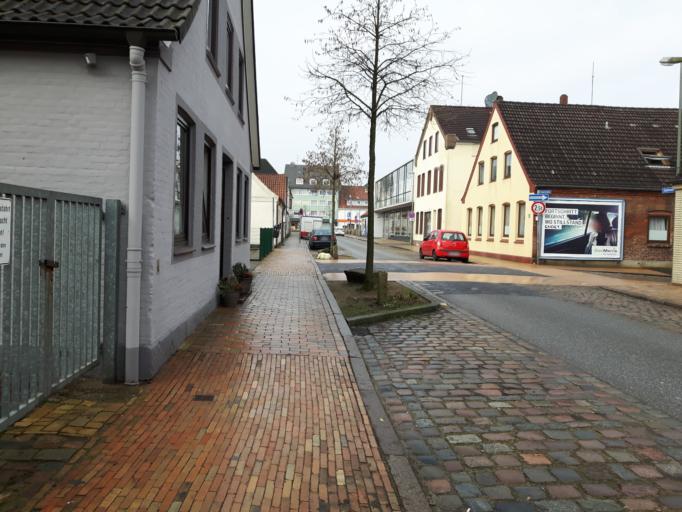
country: DE
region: Schleswig-Holstein
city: Neumunster
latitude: 54.0769
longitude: 9.9853
